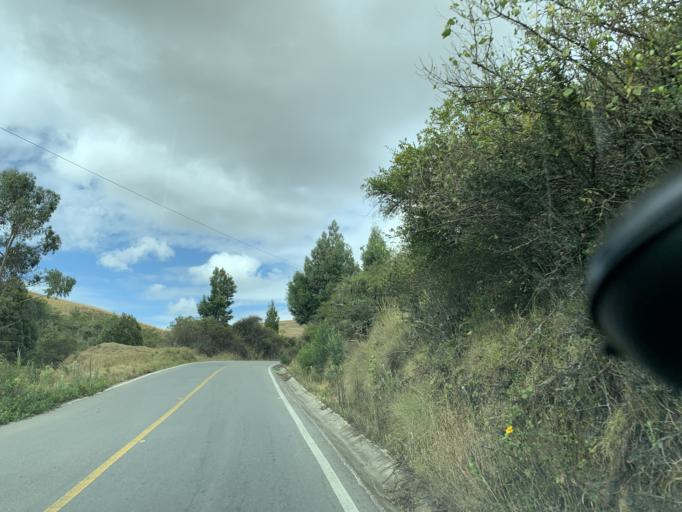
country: CO
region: Boyaca
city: Toca
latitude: 5.5717
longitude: -73.2312
